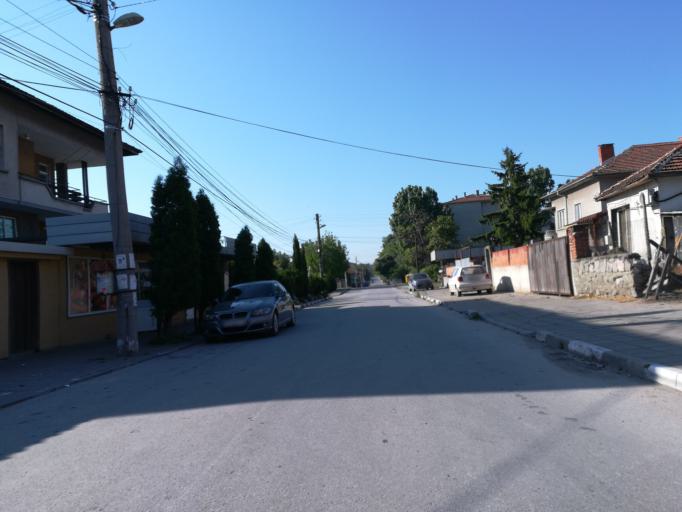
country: BG
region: Stara Zagora
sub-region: Obshtina Chirpan
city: Chirpan
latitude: 42.1062
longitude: 25.2244
